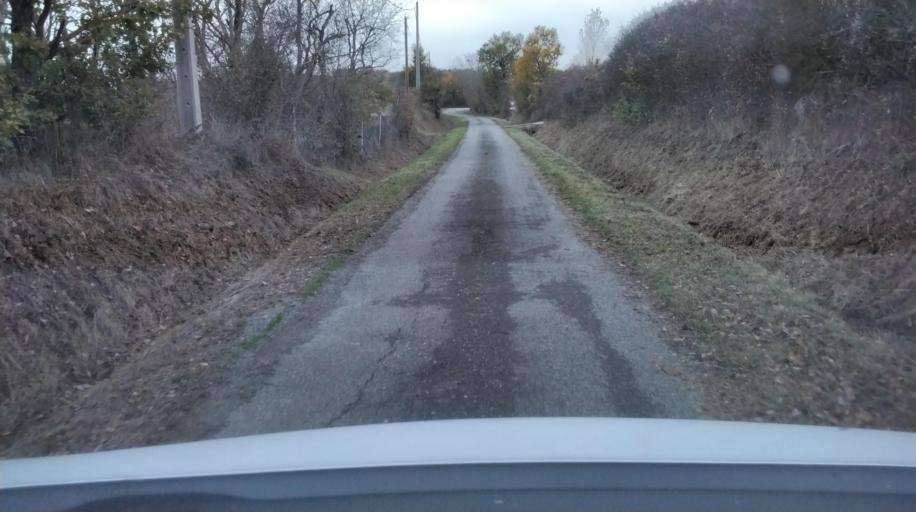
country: FR
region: Midi-Pyrenees
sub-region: Departement de la Haute-Garonne
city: Le Fousseret
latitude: 43.2725
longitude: 1.0291
